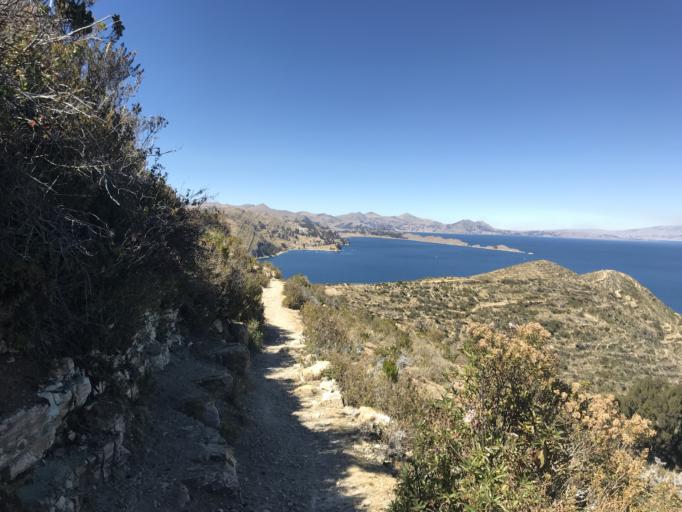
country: BO
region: La Paz
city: Yumani
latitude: -16.0432
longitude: -69.1475
